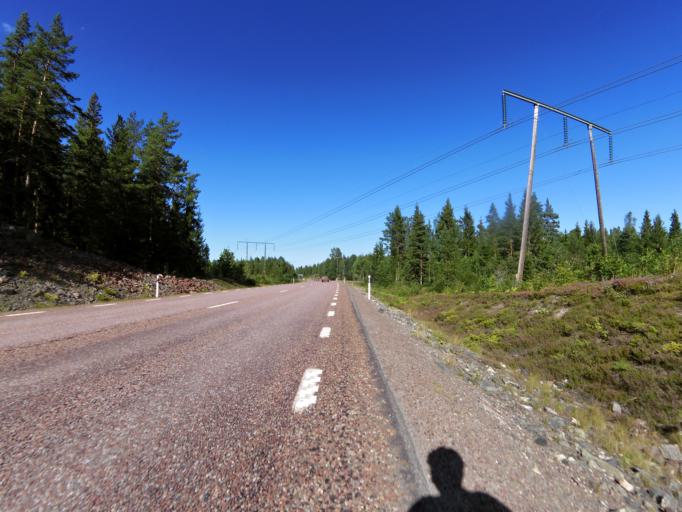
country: SE
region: Gaevleborg
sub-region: Hofors Kommun
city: Hofors
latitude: 60.5475
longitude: 16.4724
